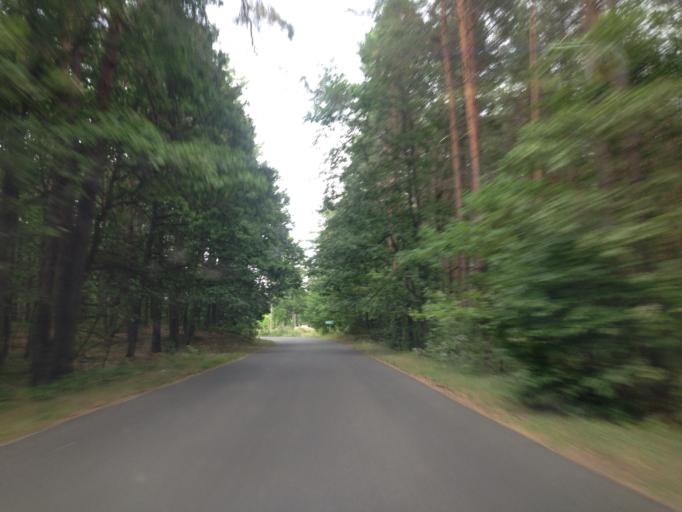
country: PL
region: Kujawsko-Pomorskie
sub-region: Powiat swiecki
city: Lniano
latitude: 53.5332
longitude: 18.1190
